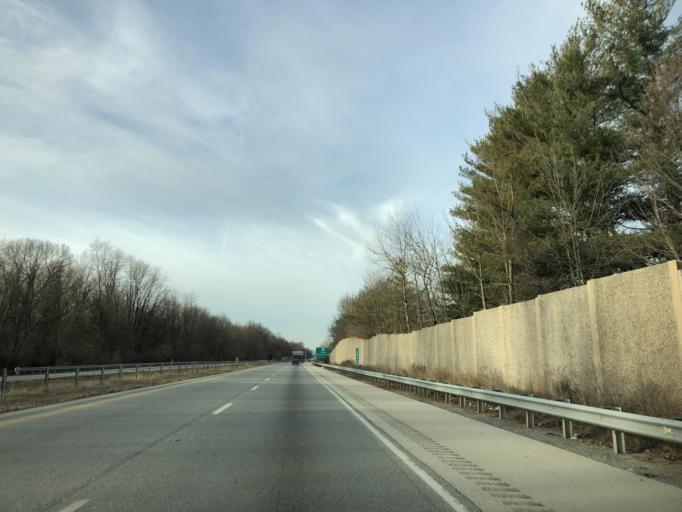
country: US
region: Pennsylvania
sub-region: Chester County
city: Exton
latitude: 40.0253
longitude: -75.6048
